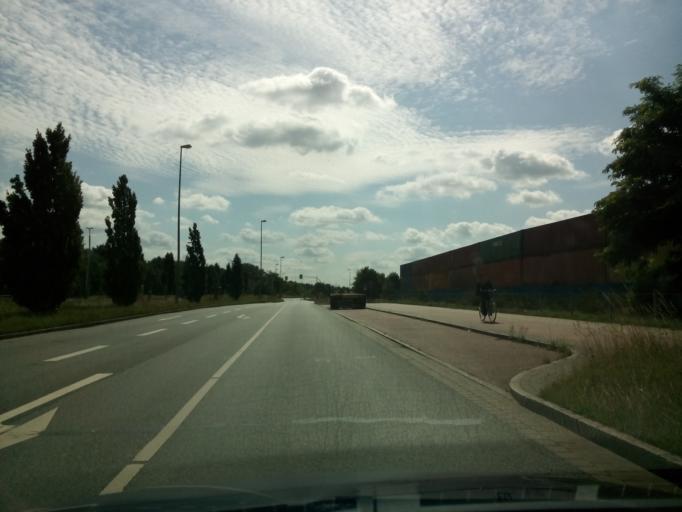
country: DE
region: Lower Saxony
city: Ritterhude
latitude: 53.1244
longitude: 8.7394
